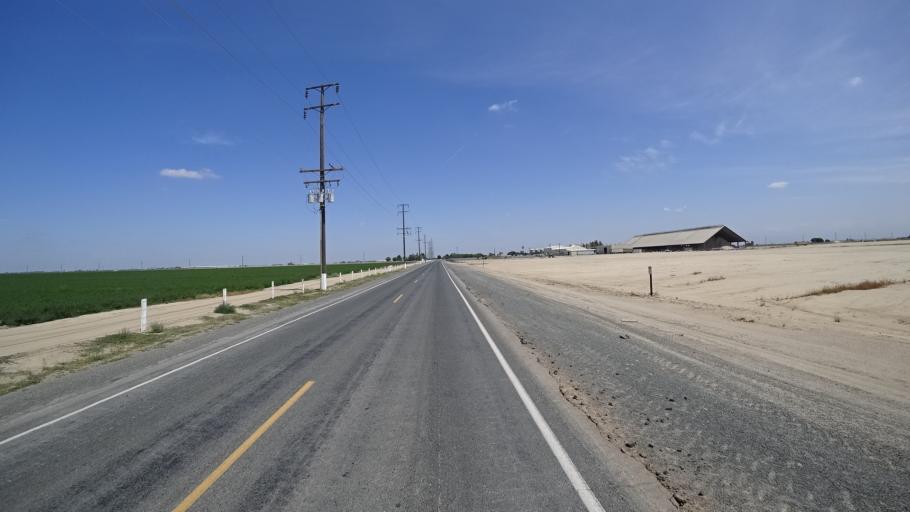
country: US
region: California
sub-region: Tulare County
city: Goshen
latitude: 36.2934
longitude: -119.4921
